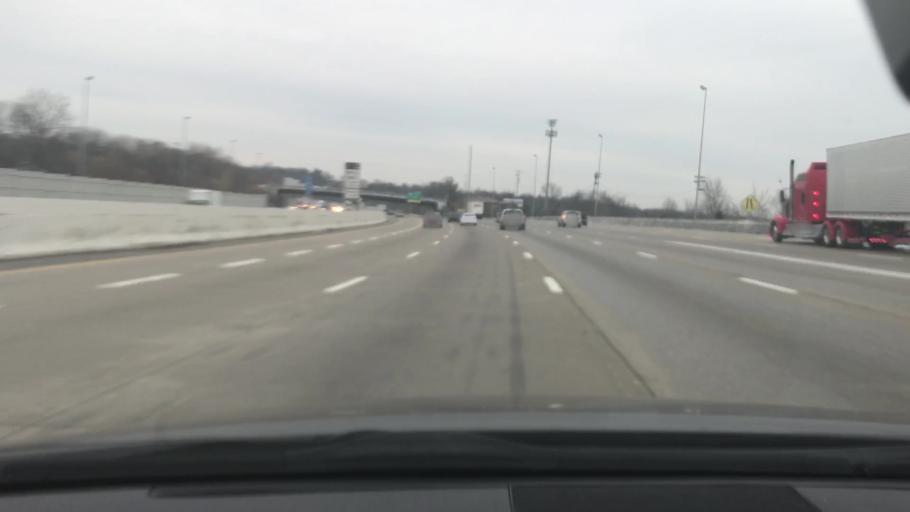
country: US
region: Tennessee
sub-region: Davidson County
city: Goodlettsville
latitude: 36.2472
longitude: -86.7435
